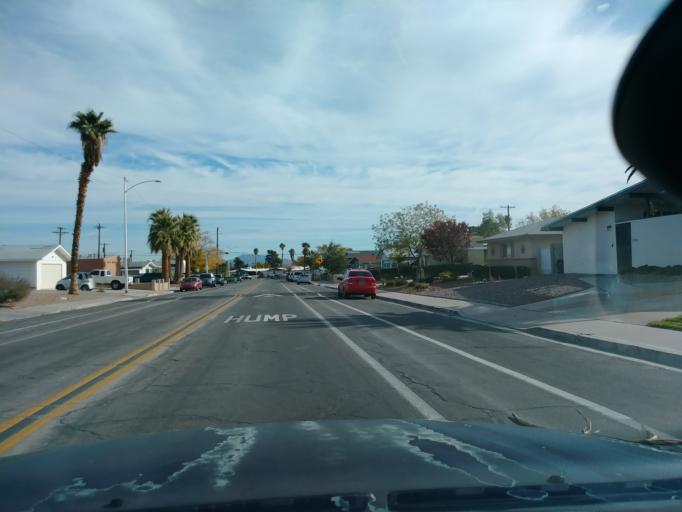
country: US
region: Nevada
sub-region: Clark County
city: Spring Valley
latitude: 36.1707
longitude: -115.2306
